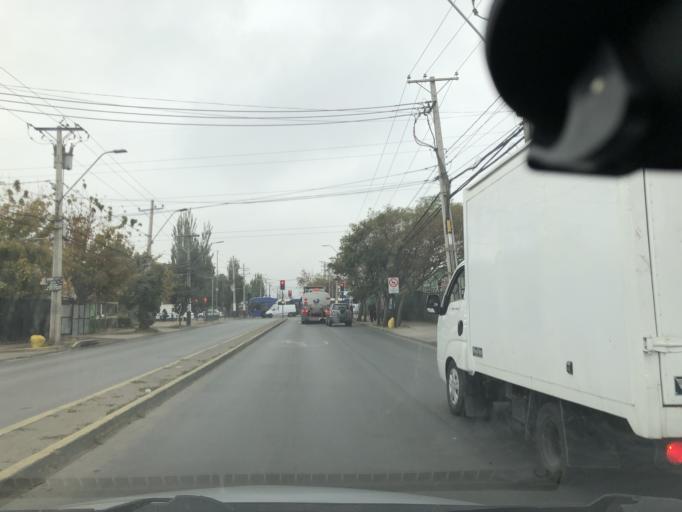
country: CL
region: Santiago Metropolitan
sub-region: Provincia de Santiago
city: La Pintana
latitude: -33.5816
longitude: -70.5984
